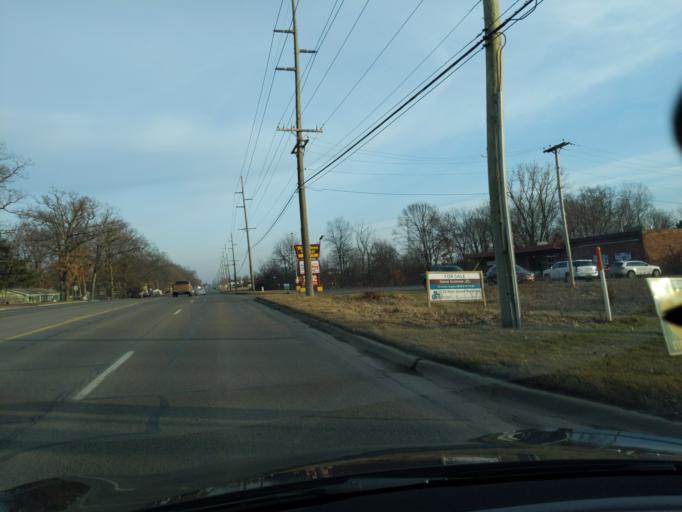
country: US
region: Michigan
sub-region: Livingston County
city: Brighton
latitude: 42.5765
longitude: -83.8428
